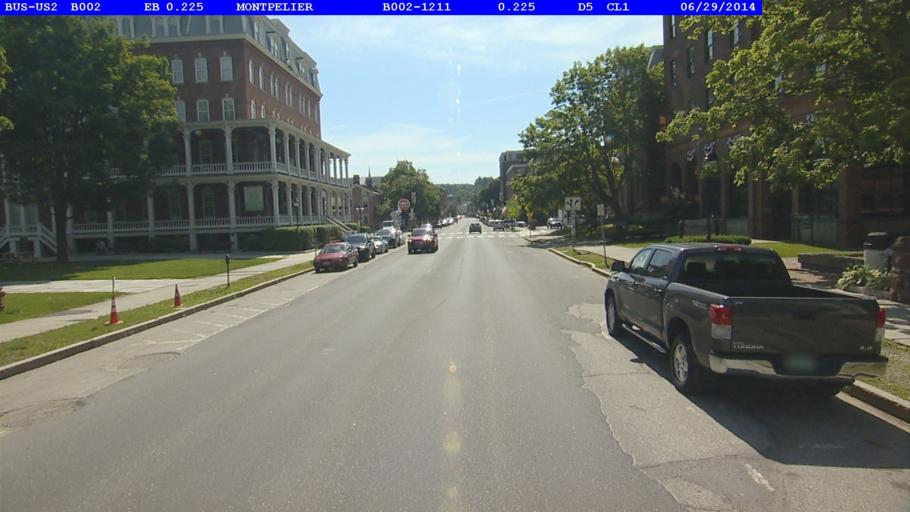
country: US
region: Vermont
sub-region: Washington County
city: Montpelier
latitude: 44.2612
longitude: -72.5803
